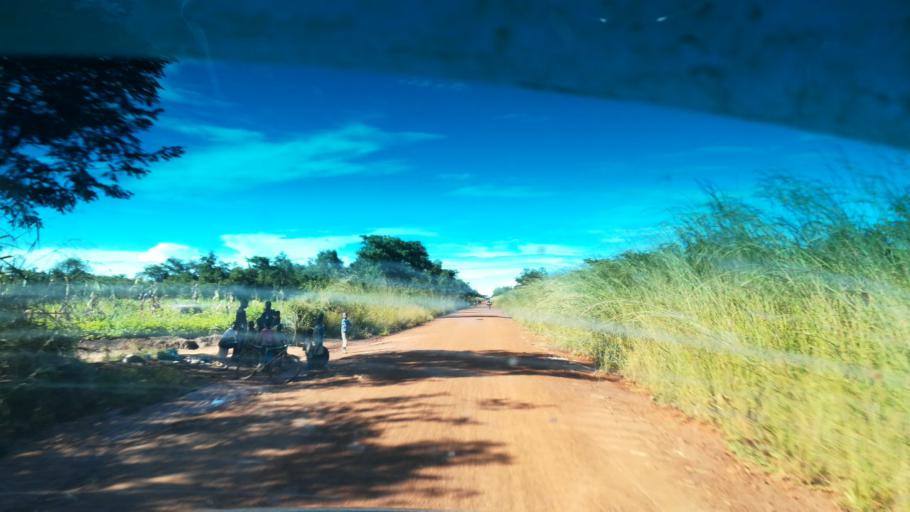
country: ZM
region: Luapula
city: Nchelenge
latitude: -9.3230
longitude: 28.2453
